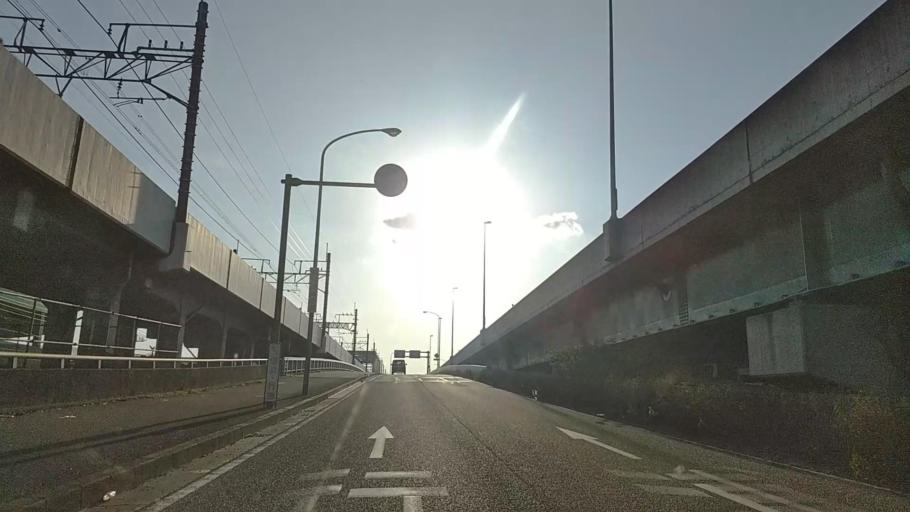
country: JP
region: Tokyo
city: Urayasu
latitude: 35.6768
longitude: 139.9331
